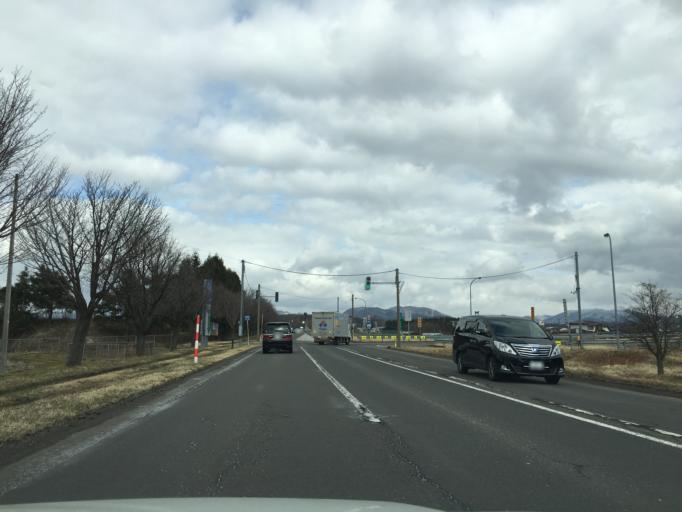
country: JP
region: Akita
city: Hanawa
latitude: 40.2562
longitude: 140.7613
